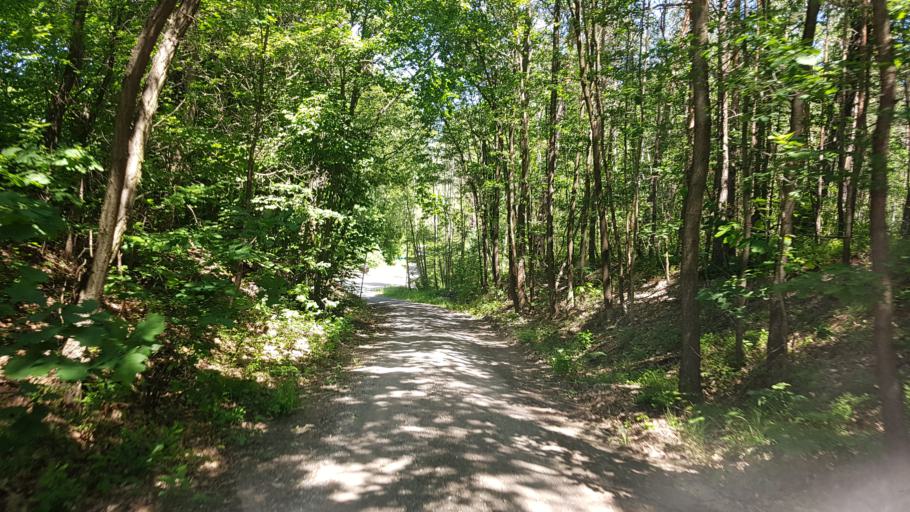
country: DE
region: Brandenburg
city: Ruckersdorf
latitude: 51.5413
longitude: 13.5761
